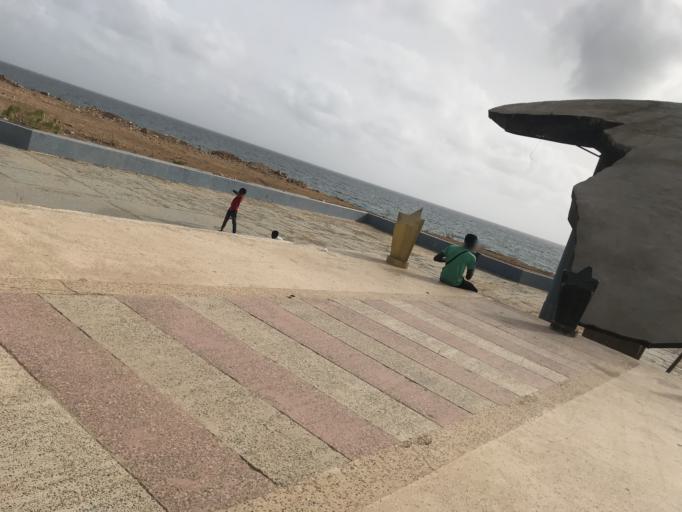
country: SN
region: Dakar
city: Mermoz Boabab
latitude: 14.6921
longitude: -17.4761
